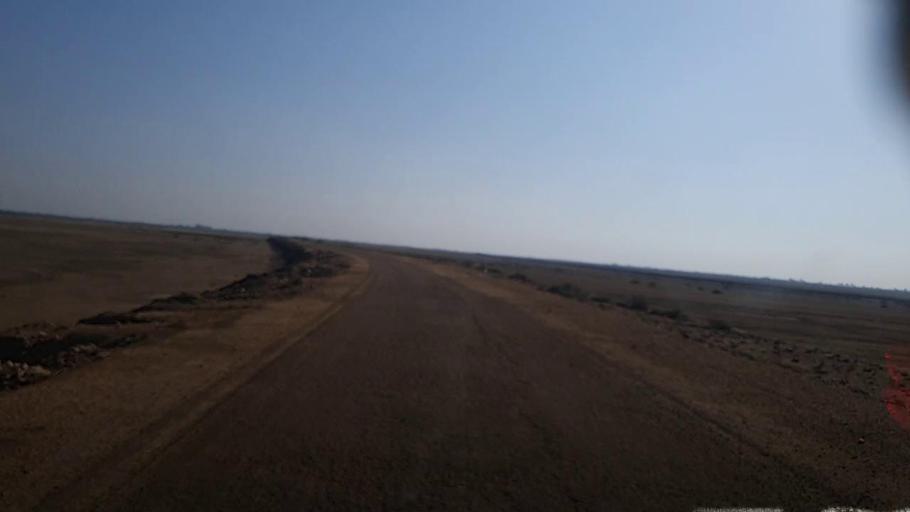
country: PK
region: Sindh
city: Mirpur Sakro
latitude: 24.5169
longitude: 67.4952
